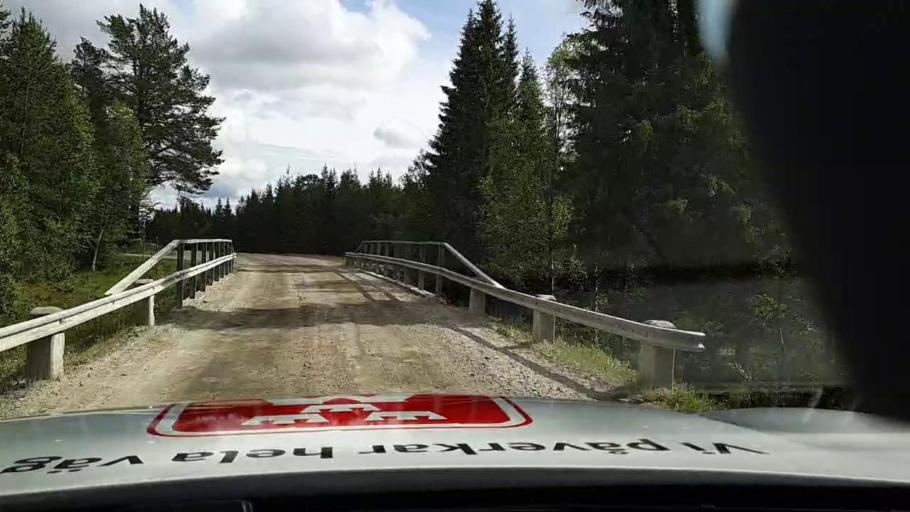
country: SE
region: Jaemtland
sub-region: Are Kommun
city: Jarpen
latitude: 62.5792
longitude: 13.3895
